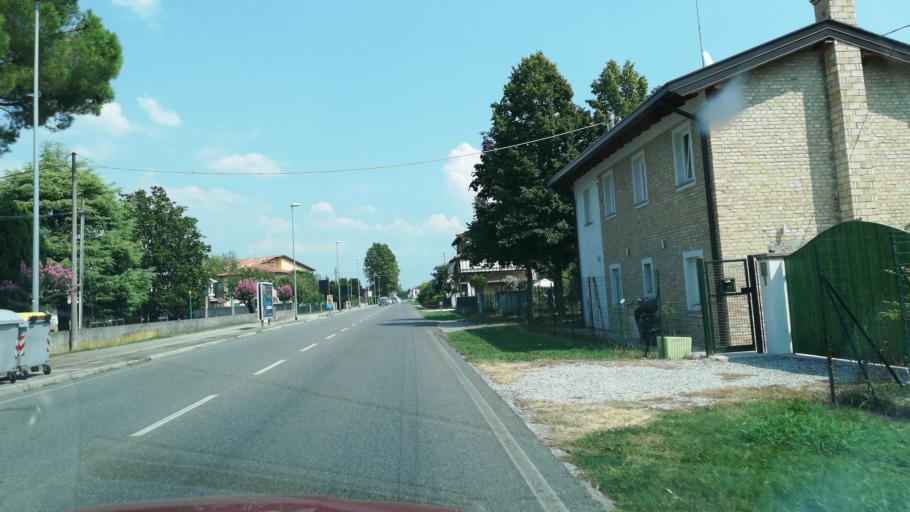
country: IT
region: Friuli Venezia Giulia
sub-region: Provincia di Udine
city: Latisana
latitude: 45.7890
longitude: 13.0137
